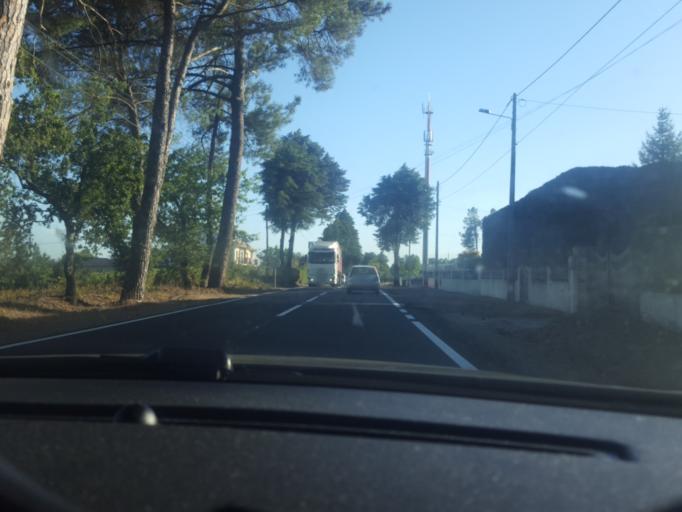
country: PT
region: Viseu
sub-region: Mangualde
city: Mangualde
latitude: 40.5839
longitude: -7.8051
